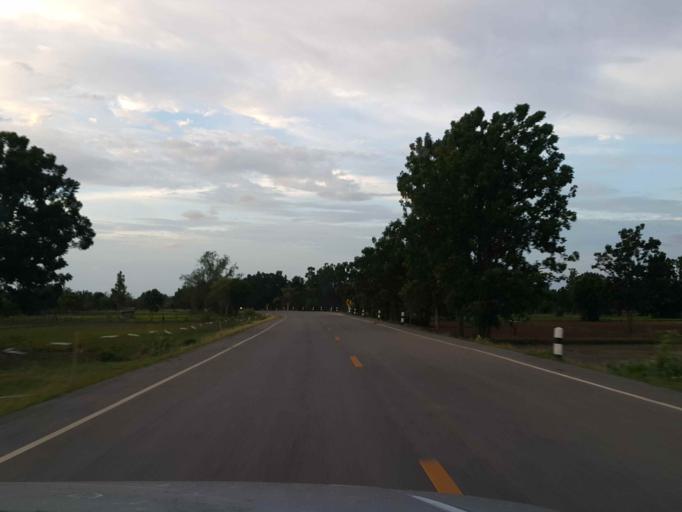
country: TH
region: Sukhothai
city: Ban Dan Lan Hoi
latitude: 17.0804
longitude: 99.5907
